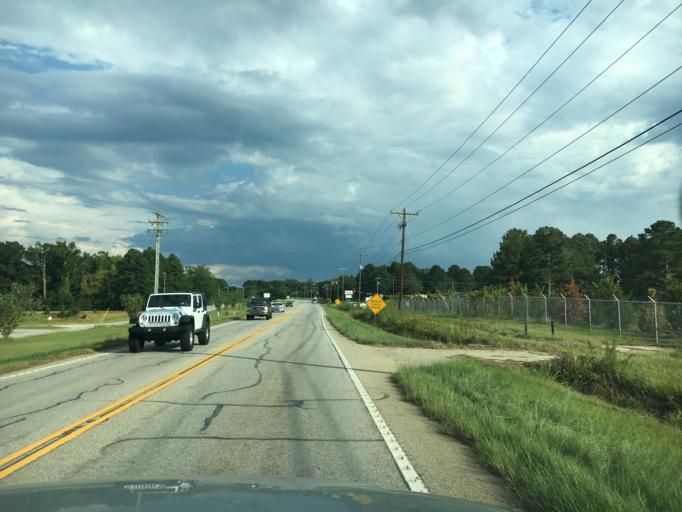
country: US
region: South Carolina
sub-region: Greenwood County
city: Ninety Six
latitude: 34.2331
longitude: -82.0607
